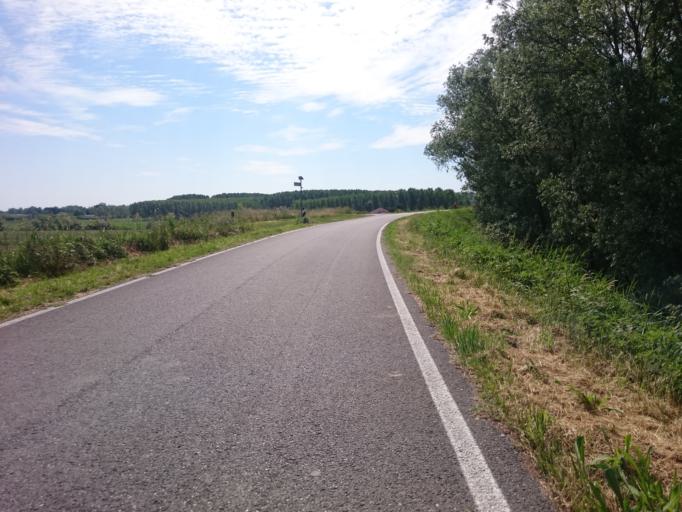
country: IT
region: Veneto
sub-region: Provincia di Rovigo
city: Corbola
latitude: 44.9739
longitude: 12.0808
